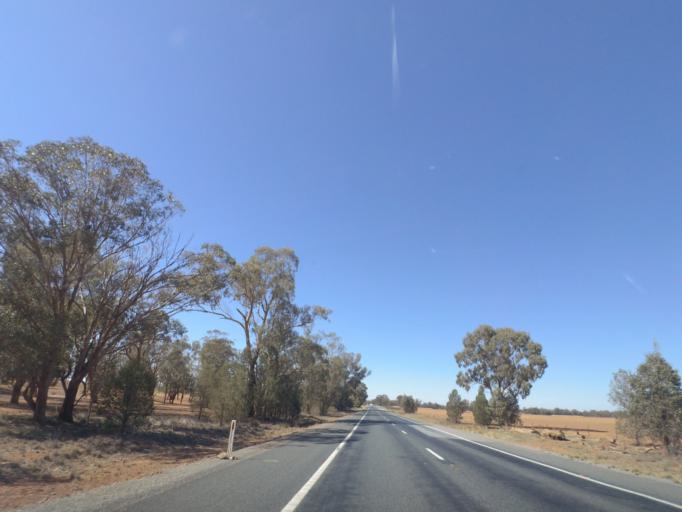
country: AU
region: New South Wales
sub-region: Bland
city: West Wyalong
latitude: -34.1866
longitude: 147.1124
